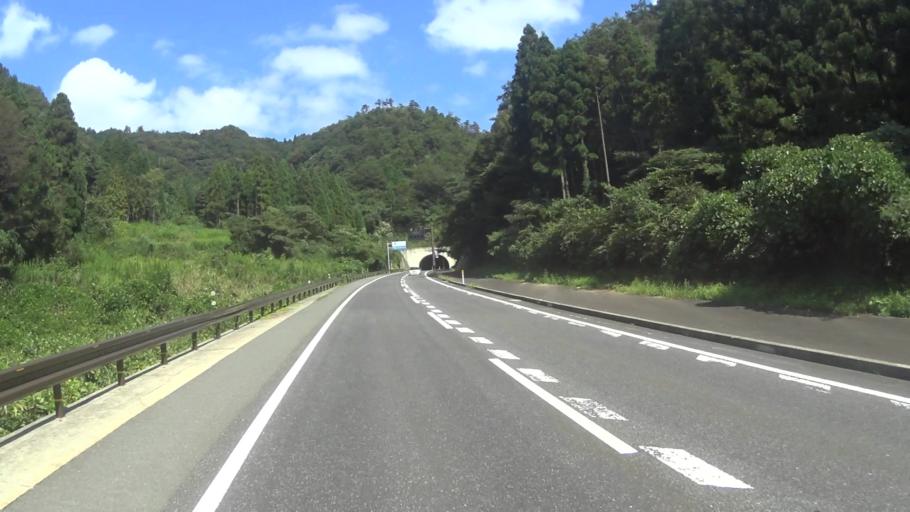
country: JP
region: Kyoto
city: Miyazu
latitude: 35.6764
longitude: 135.2749
